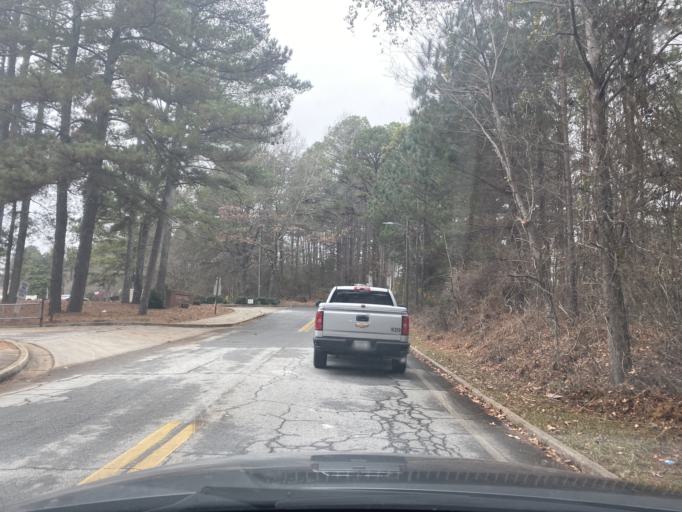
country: US
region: Georgia
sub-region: DeKalb County
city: Pine Mountain
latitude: 33.6966
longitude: -84.1635
